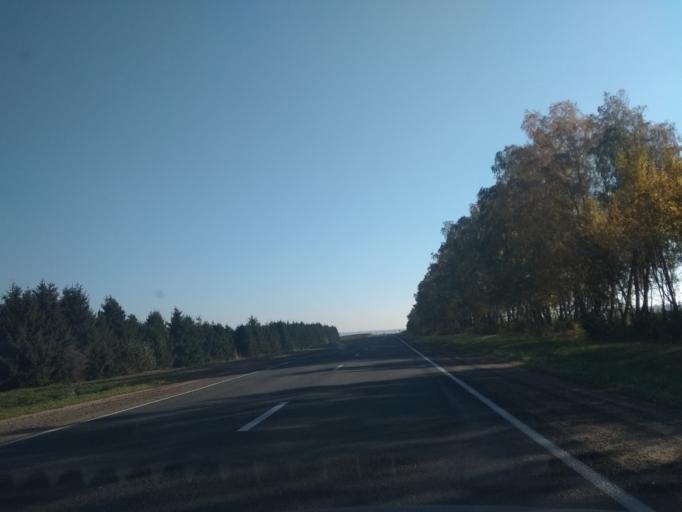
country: BY
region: Grodnenskaya
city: Slonim
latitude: 53.1206
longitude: 25.1072
